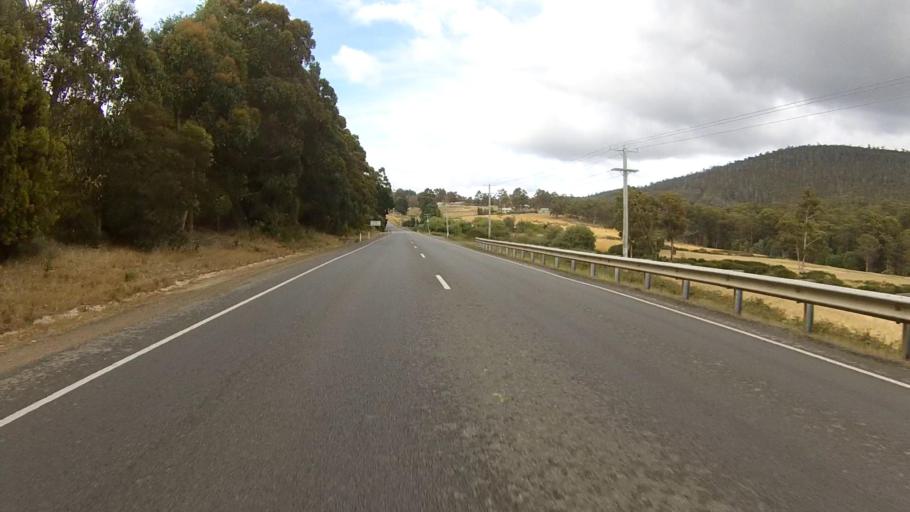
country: AU
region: Tasmania
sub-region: Kingborough
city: Kettering
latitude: -43.0829
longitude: 147.2536
